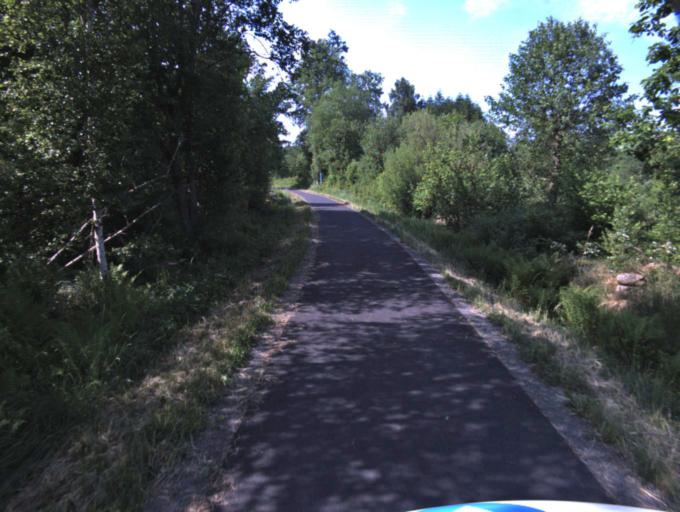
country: SE
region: Skane
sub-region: Kristianstads Kommun
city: Tollarp
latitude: 56.1975
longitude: 14.2889
